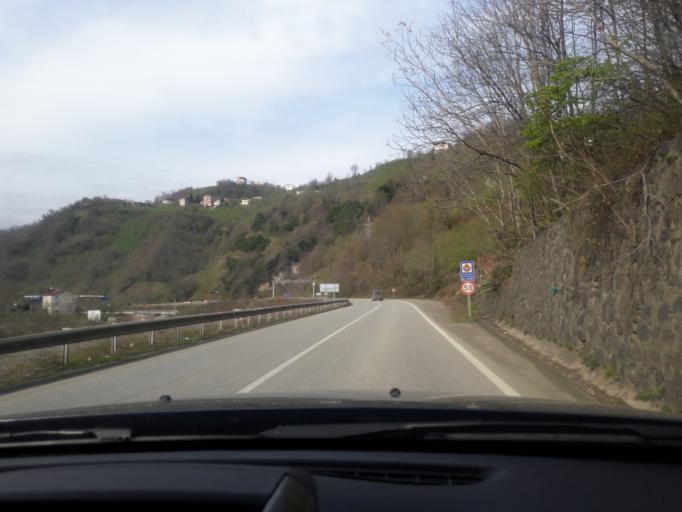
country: TR
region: Trabzon
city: Besikduzu
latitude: 41.0578
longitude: 39.2126
